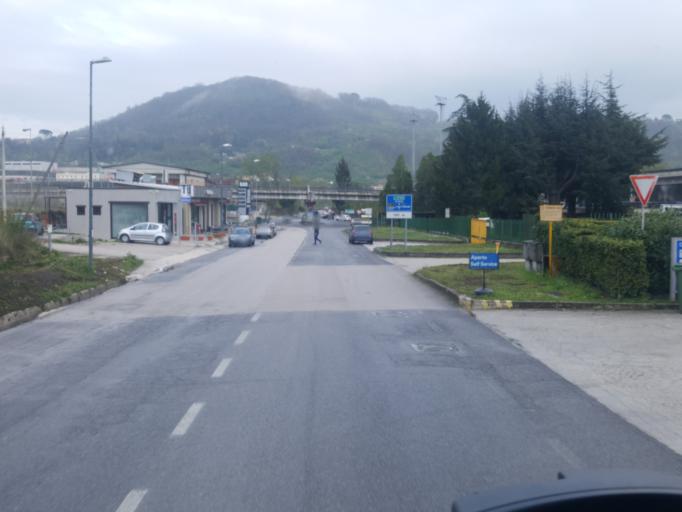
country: IT
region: Campania
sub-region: Provincia di Avellino
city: Atripalda
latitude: 40.9386
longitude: 14.8242
